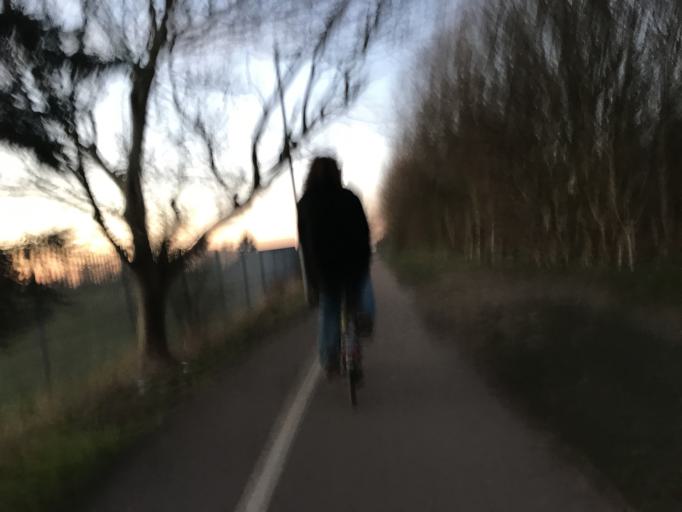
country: GB
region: England
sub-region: Lincolnshire
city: Holton le Clay
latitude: 53.5234
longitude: -0.0770
